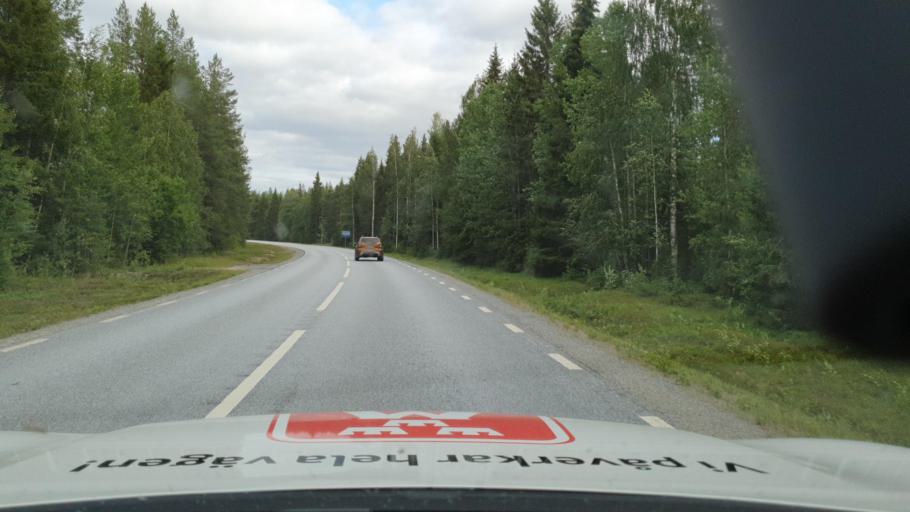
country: SE
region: Vaesterbotten
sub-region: Bjurholms Kommun
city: Bjurholm
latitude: 63.9374
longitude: 18.9352
